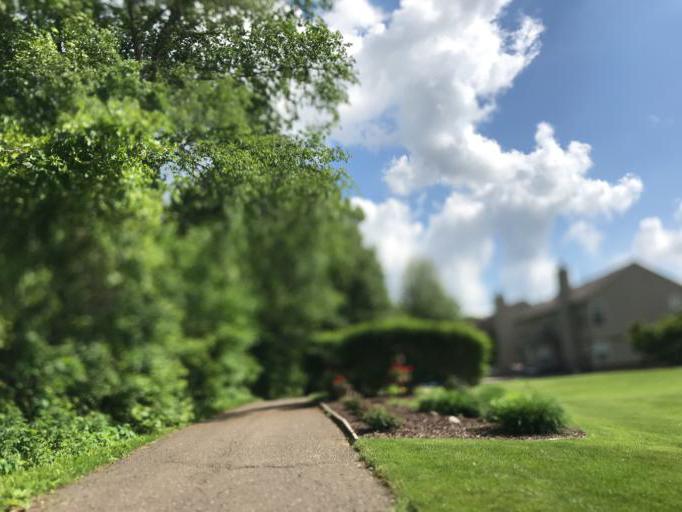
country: US
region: Michigan
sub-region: Oakland County
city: South Lyon
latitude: 42.4485
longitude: -83.6604
